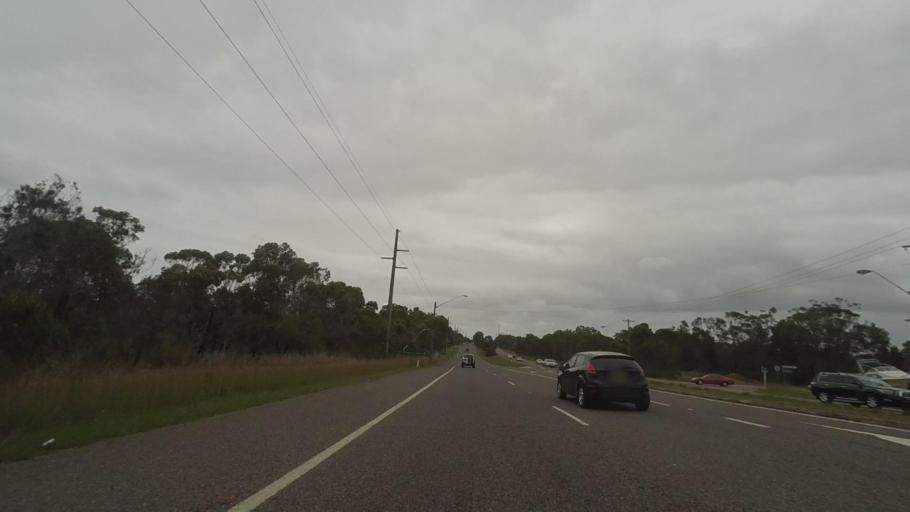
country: AU
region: New South Wales
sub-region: Wyong Shire
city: Kingfisher Shores
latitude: -33.1863
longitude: 151.5848
